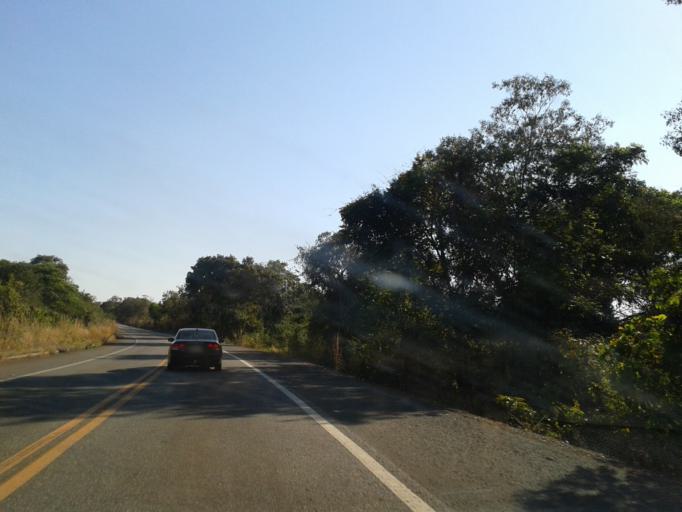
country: BR
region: Goias
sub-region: Mozarlandia
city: Mozarlandia
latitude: -14.8217
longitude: -50.5307
